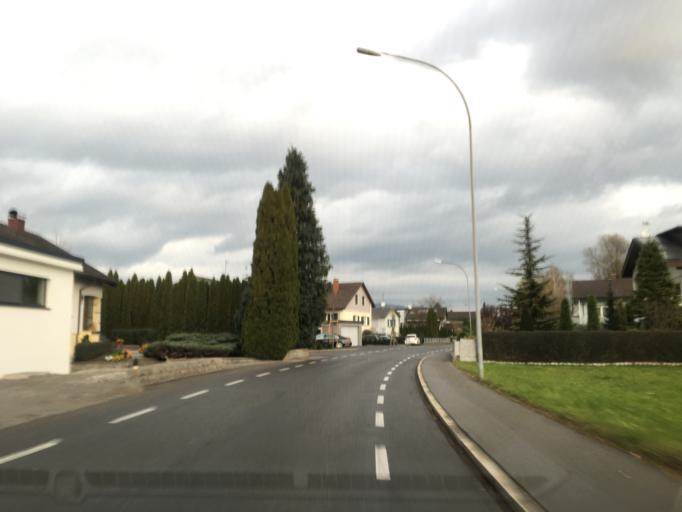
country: AT
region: Vorarlberg
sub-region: Politischer Bezirk Feldkirch
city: Gotzis
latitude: 47.3397
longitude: 9.6252
